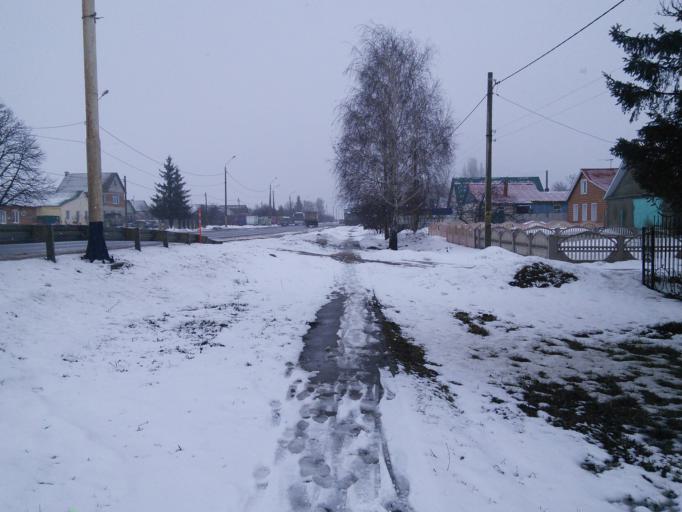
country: RU
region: Kursk
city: Chernitsyno
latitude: 51.5790
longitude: 36.0805
